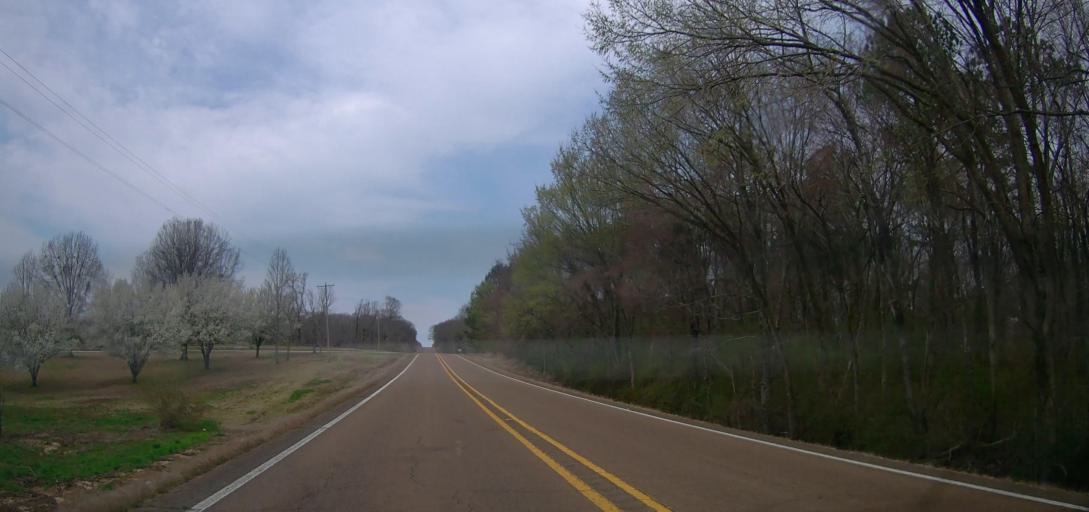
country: US
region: Mississippi
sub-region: Marshall County
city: Byhalia
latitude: 34.8334
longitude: -89.5803
